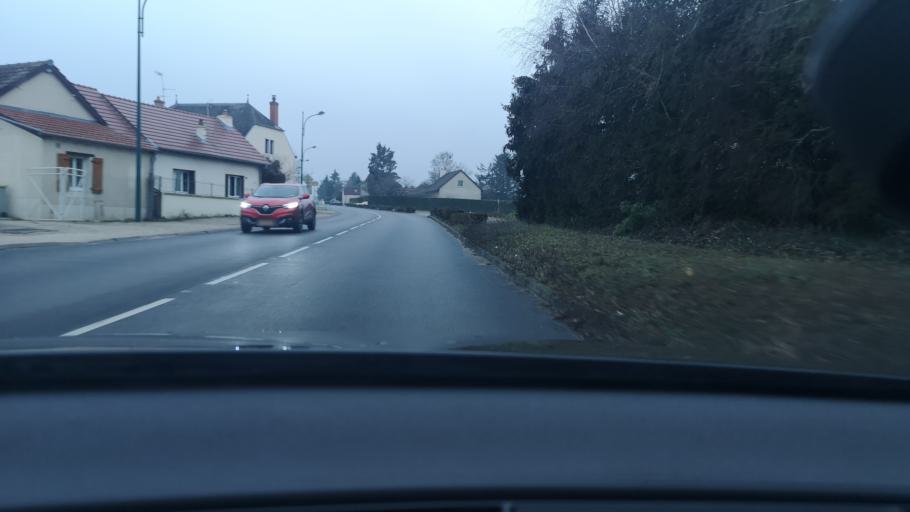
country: FR
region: Bourgogne
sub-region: Departement de la Cote-d'Or
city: Fenay
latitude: 47.1917
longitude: 5.0799
